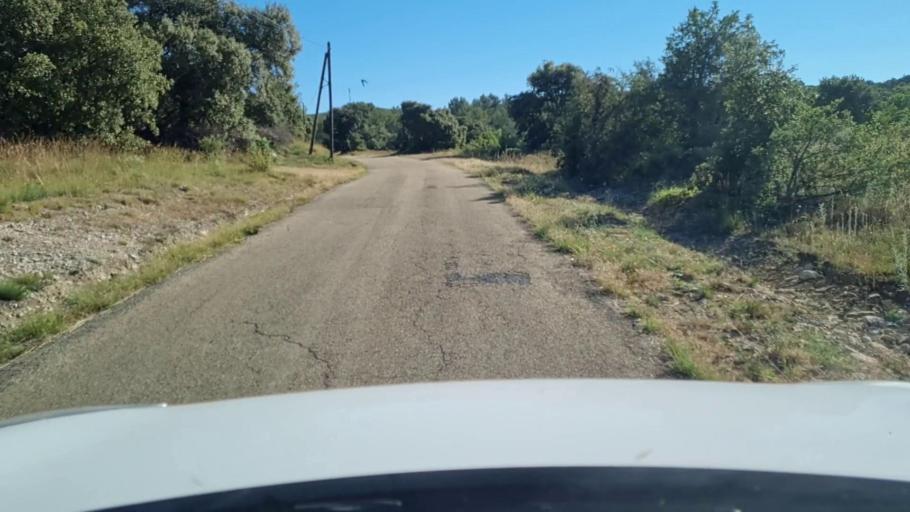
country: FR
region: Languedoc-Roussillon
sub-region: Departement du Gard
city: Villevieille
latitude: 43.8430
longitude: 4.0770
